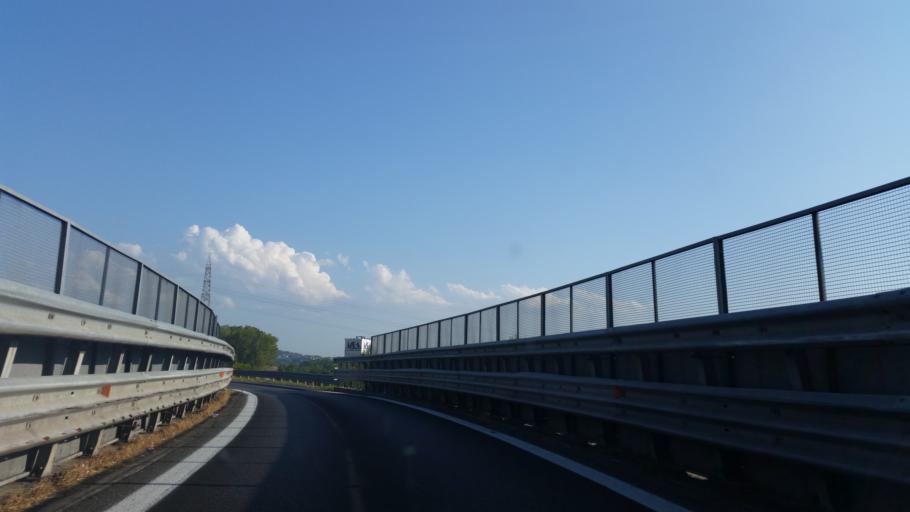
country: IT
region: Piedmont
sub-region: Provincia di Asti
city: Asti
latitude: 44.9063
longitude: 8.2442
